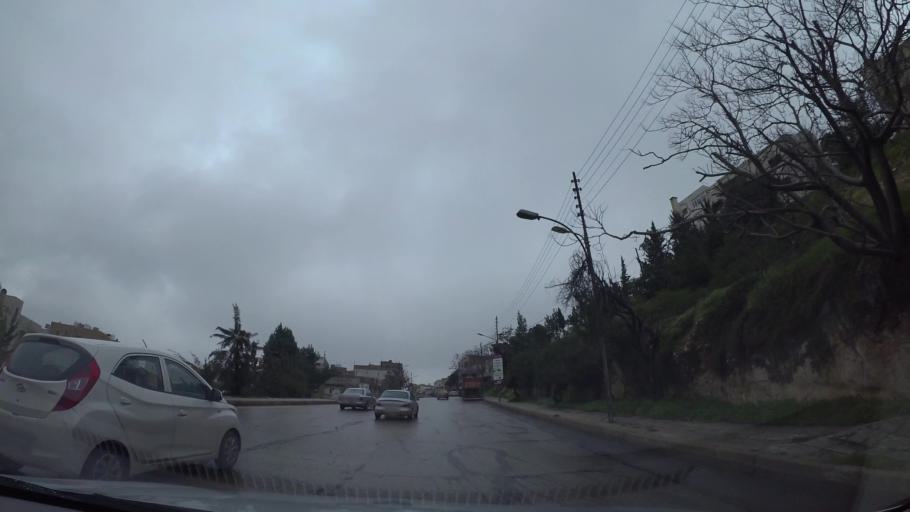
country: JO
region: Amman
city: Al Jubayhah
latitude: 32.0281
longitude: 35.8334
